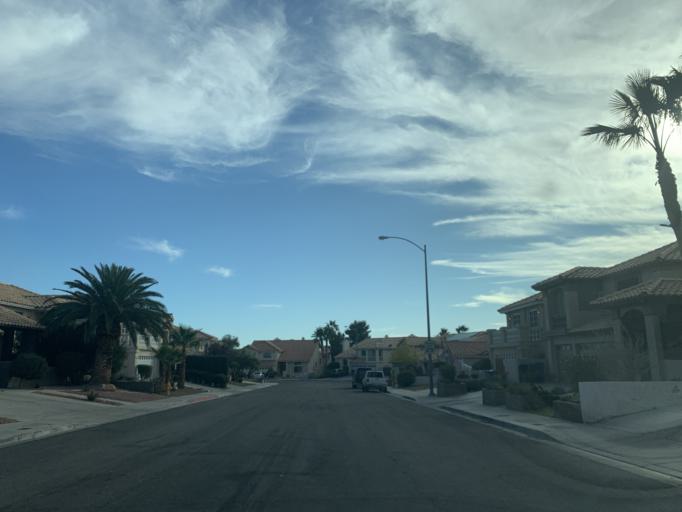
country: US
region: Nevada
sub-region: Clark County
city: Summerlin South
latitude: 36.1293
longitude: -115.3035
